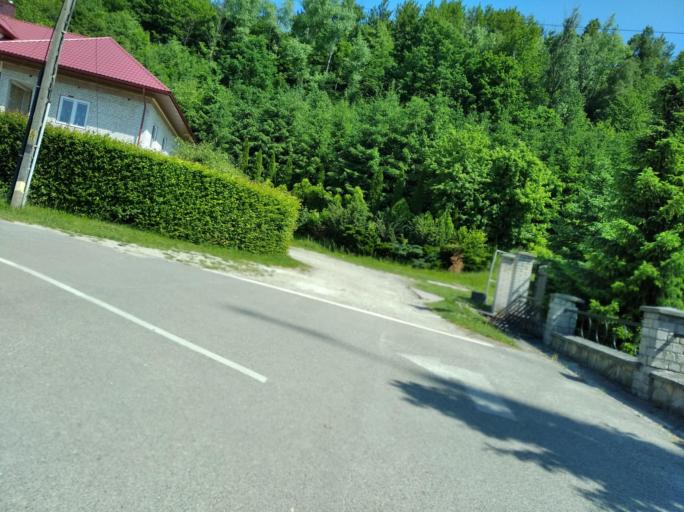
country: PL
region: Subcarpathian Voivodeship
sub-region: Powiat ropczycko-sedziszowski
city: Zagorzyce
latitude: 50.0099
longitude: 21.6596
